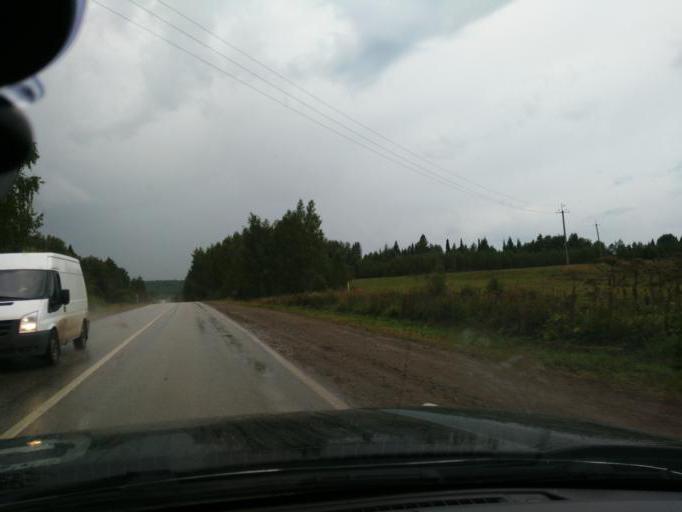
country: RU
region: Perm
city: Barda
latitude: 56.8851
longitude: 55.8293
